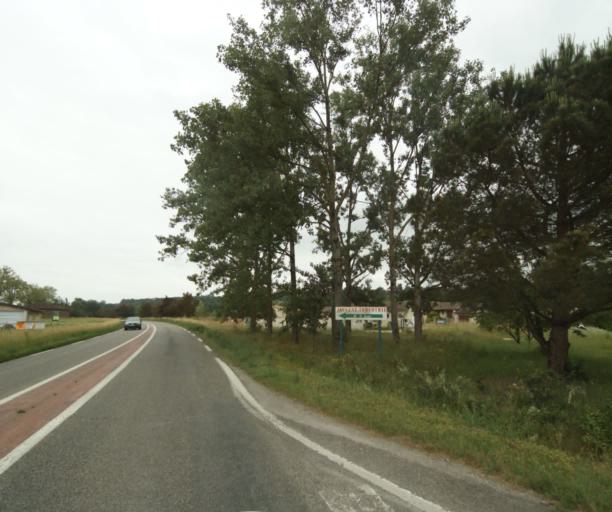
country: FR
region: Midi-Pyrenees
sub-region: Departement du Tarn-et-Garonne
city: Saint-Nauphary
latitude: 43.9812
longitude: 1.3936
